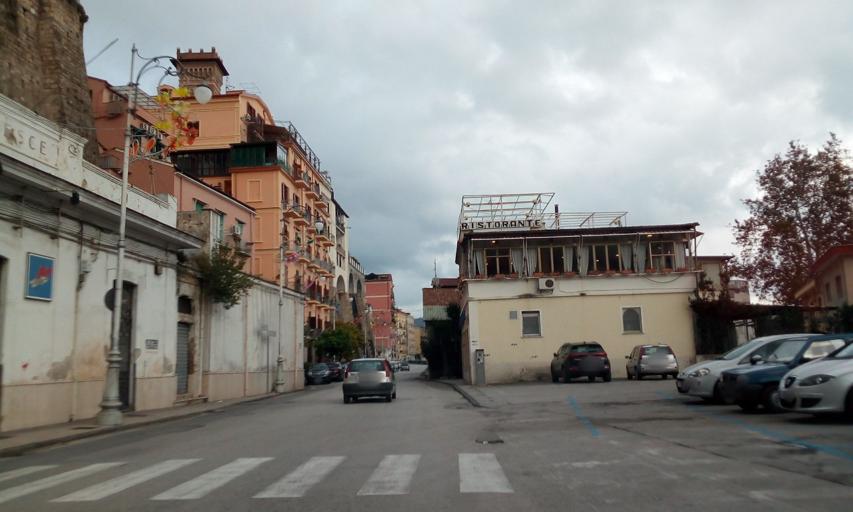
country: IT
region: Campania
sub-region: Provincia di Salerno
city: Vietri sul Mare
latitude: 40.6779
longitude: 14.7454
